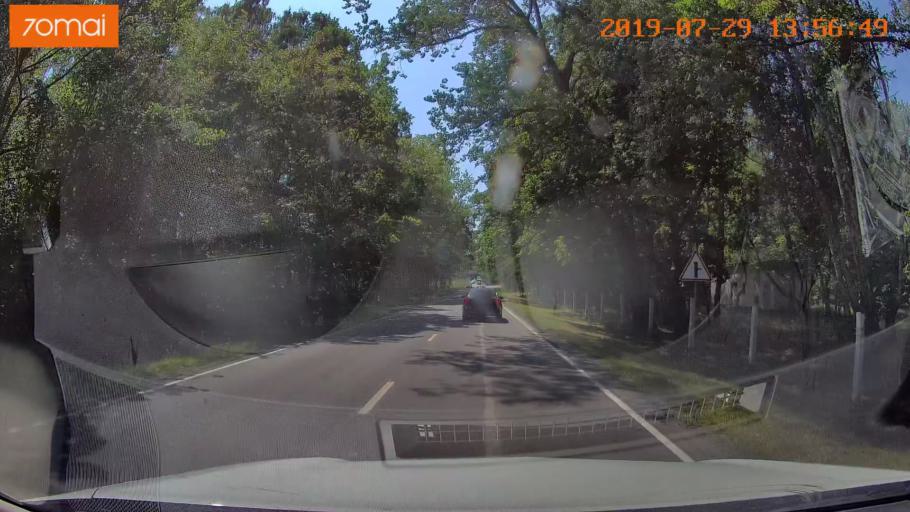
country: RU
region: Kaliningrad
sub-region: Gorod Kaliningrad
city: Baltiysk
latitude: 54.7057
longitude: 19.9464
